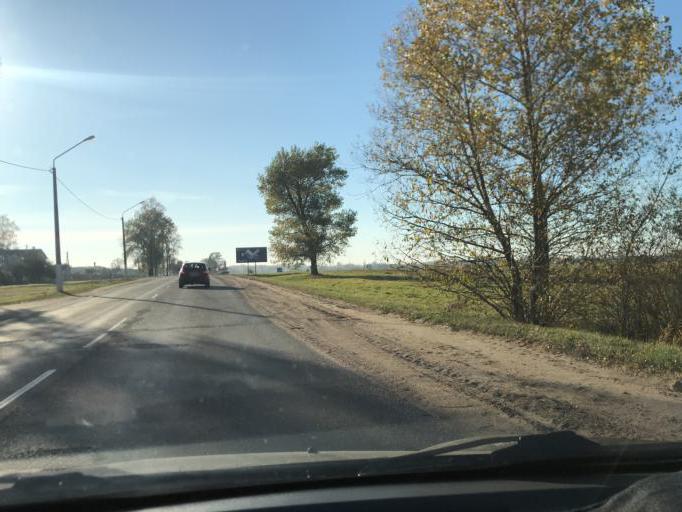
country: BY
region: Minsk
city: Slutsk
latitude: 53.0488
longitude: 27.6223
